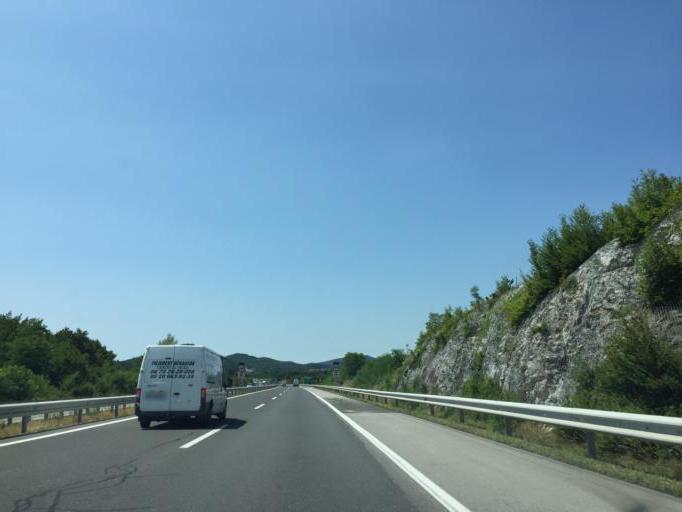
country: SI
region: Sezana
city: Sezana
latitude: 45.7128
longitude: 13.9066
